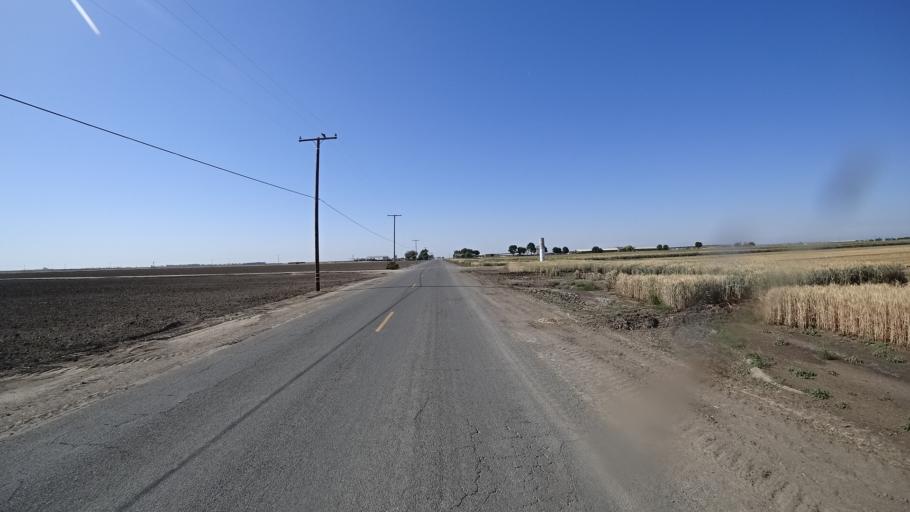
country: US
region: California
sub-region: Kings County
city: Home Garden
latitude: 36.2522
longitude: -119.5473
